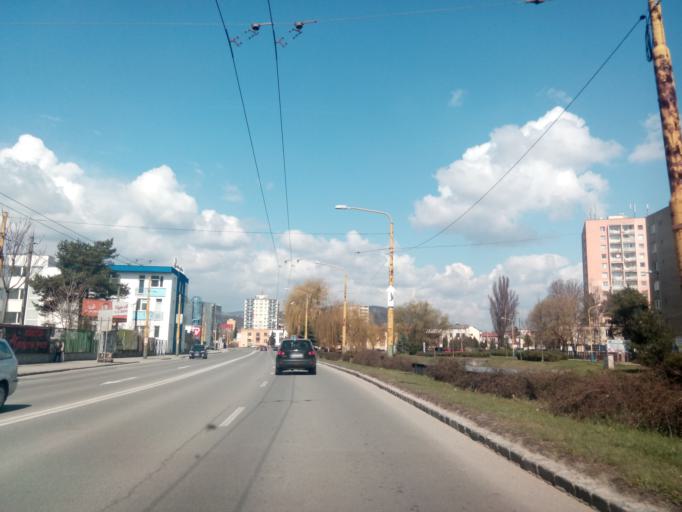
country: SK
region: Kosicky
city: Kosice
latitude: 48.7297
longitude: 21.2559
